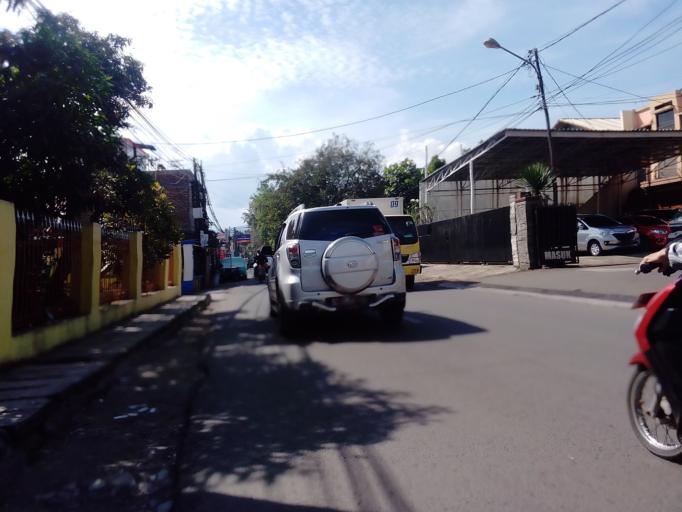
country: ID
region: West Java
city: Bandung
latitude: -6.9422
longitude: 107.6636
